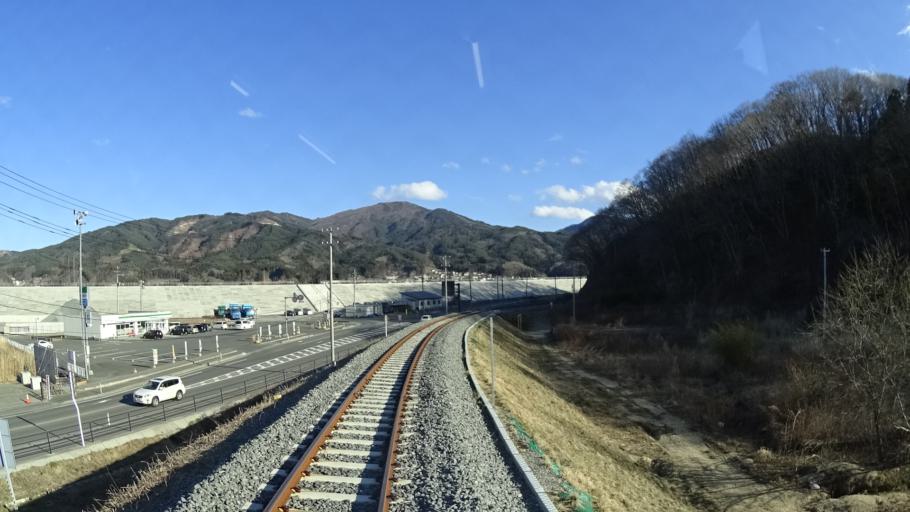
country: JP
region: Iwate
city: Miyako
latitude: 39.5908
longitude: 141.9454
